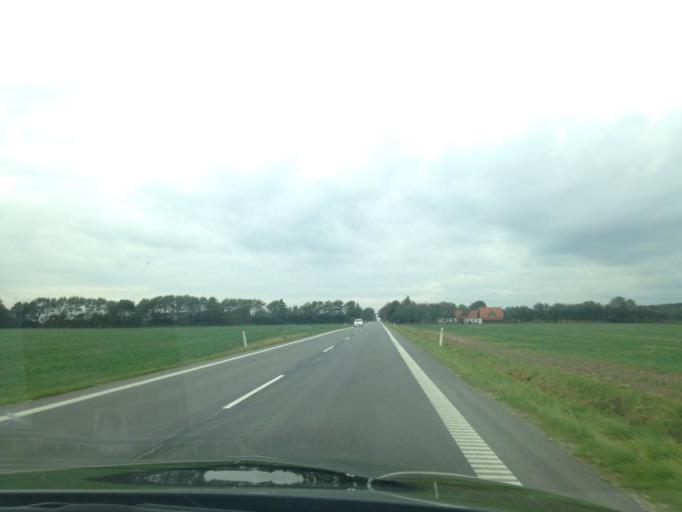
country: DK
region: South Denmark
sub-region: Kolding Kommune
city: Christiansfeld
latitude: 55.4122
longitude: 9.4775
